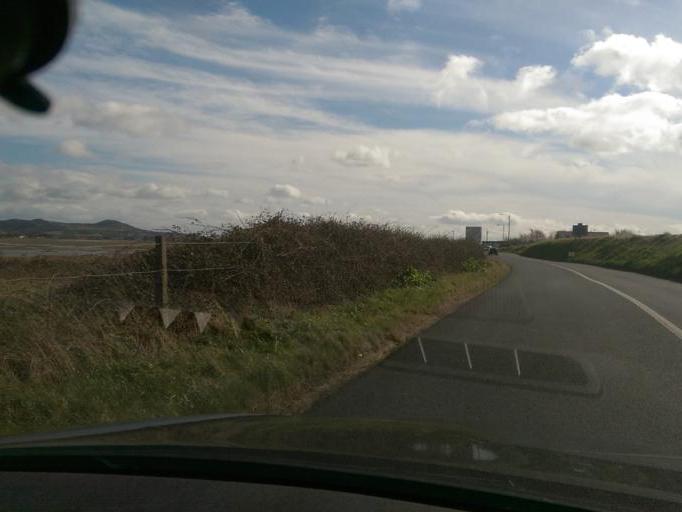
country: IE
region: Leinster
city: Portmarnock
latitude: 53.4115
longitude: -6.1371
